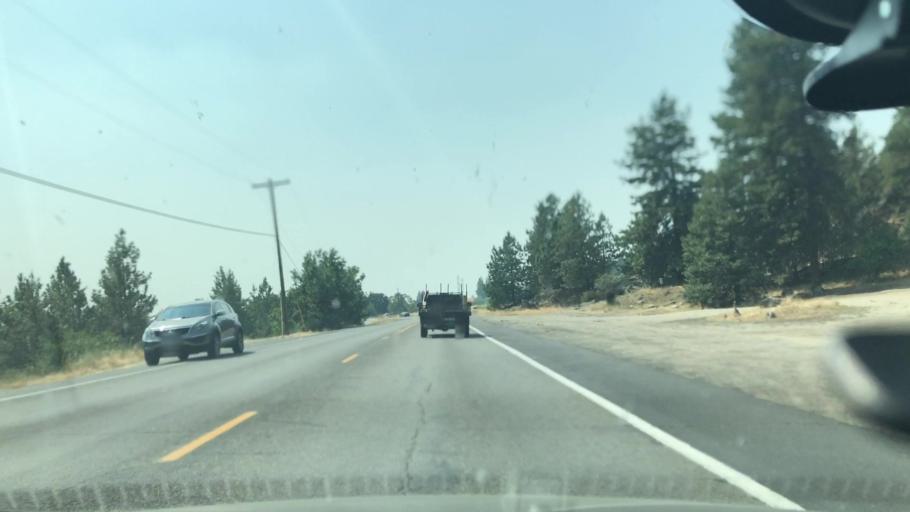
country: US
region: Washington
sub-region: Spokane County
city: Millwood
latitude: 47.6869
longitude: -117.3278
